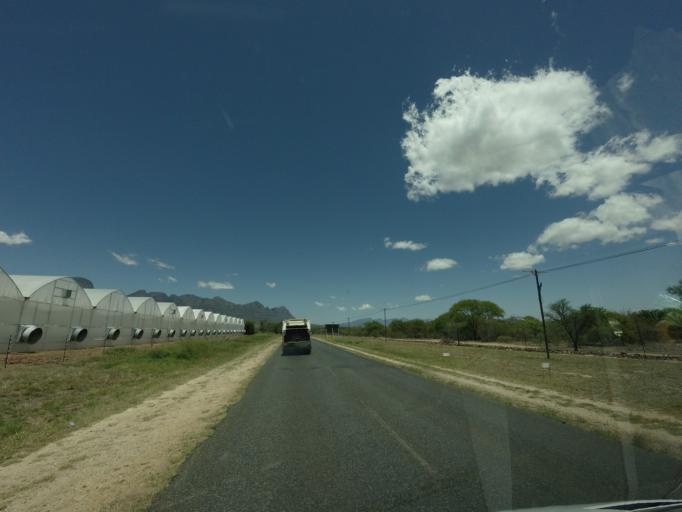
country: ZA
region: Limpopo
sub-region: Mopani District Municipality
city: Hoedspruit
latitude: -24.3969
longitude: 30.8149
